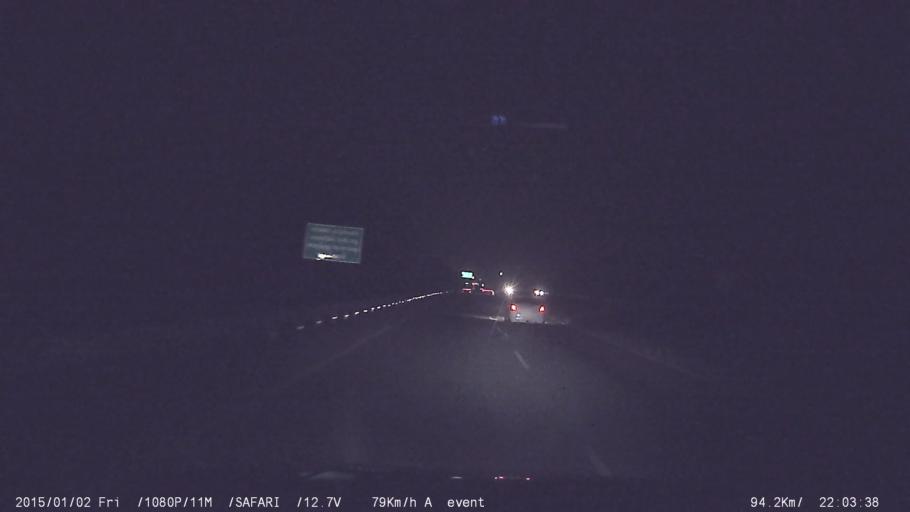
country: IN
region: Tamil Nadu
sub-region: Vellore
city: Walajapet
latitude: 12.9060
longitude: 79.4144
